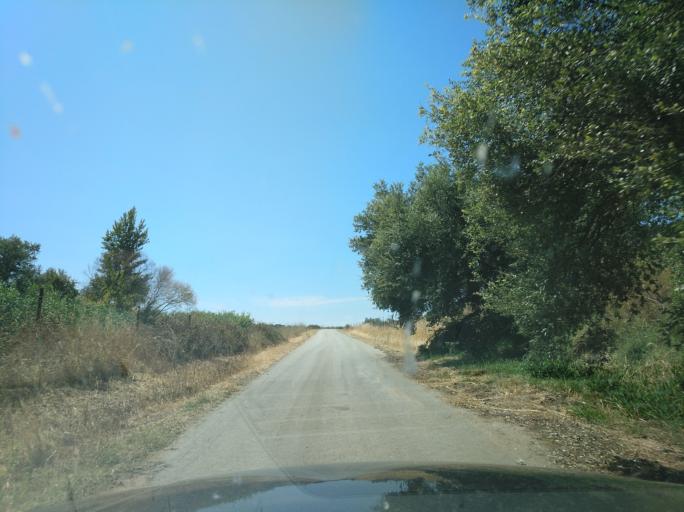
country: PT
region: Portalegre
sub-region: Campo Maior
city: Campo Maior
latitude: 38.9597
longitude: -7.1018
